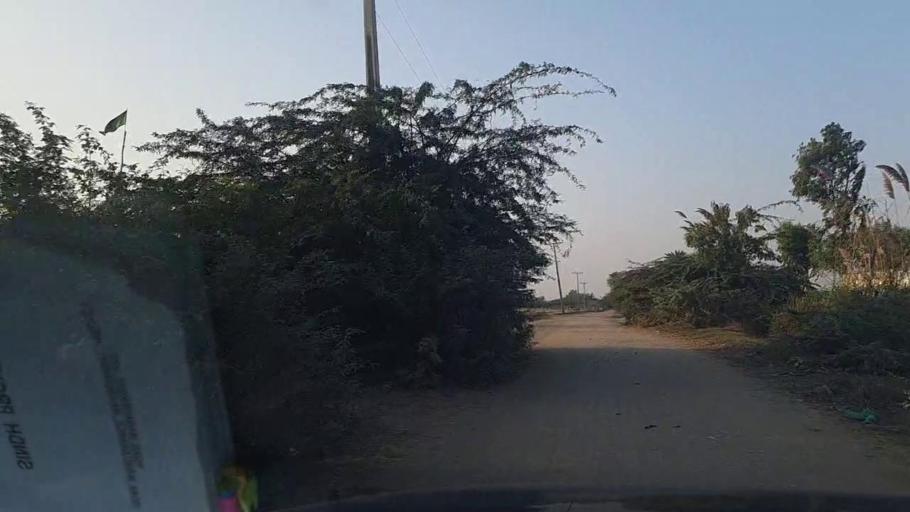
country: PK
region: Sindh
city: Keti Bandar
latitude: 24.3062
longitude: 67.6037
